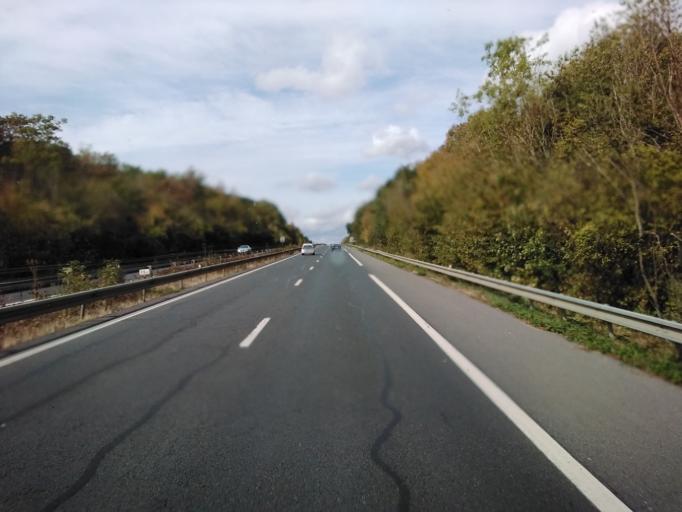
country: FR
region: Champagne-Ardenne
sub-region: Departement des Ardennes
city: Lumes
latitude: 49.7317
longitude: 4.8055
